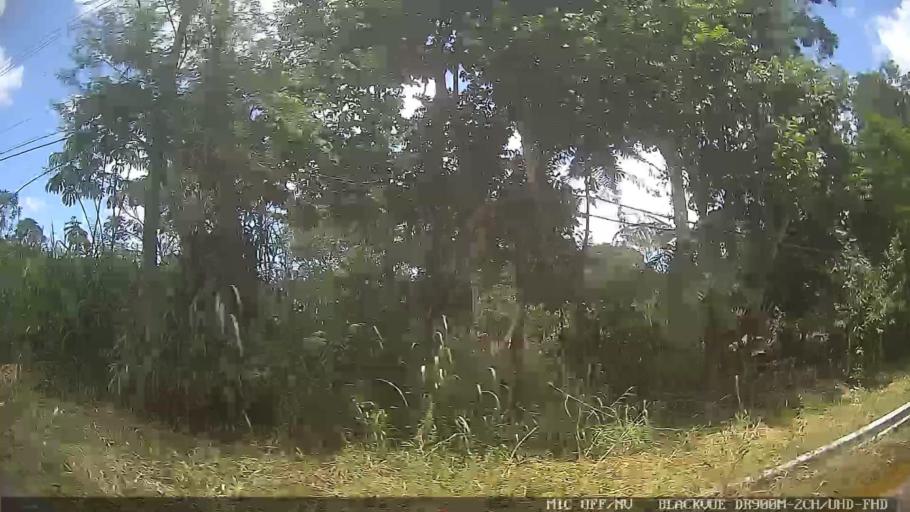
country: BR
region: Sao Paulo
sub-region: Jacarei
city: Jacarei
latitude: -23.3127
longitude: -45.9269
